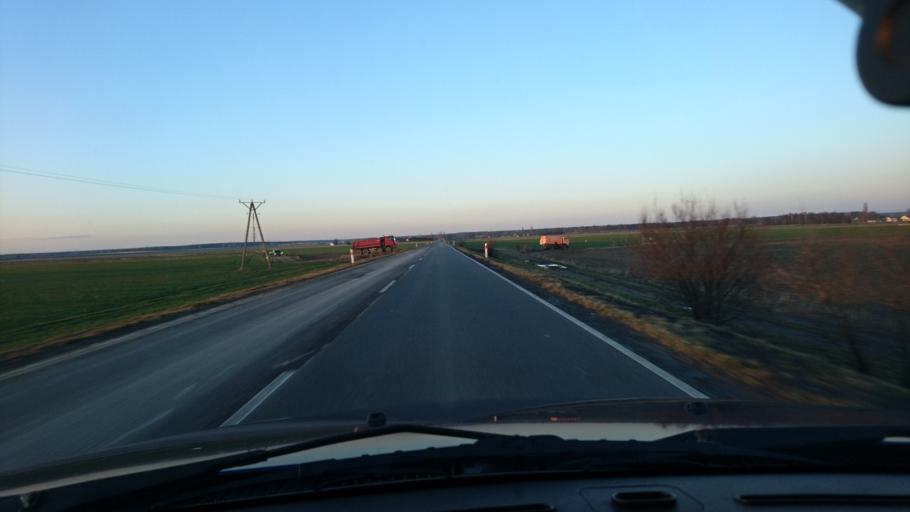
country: PL
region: Silesian Voivodeship
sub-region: Powiat gliwicki
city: Wielowies
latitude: 50.5117
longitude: 18.6048
